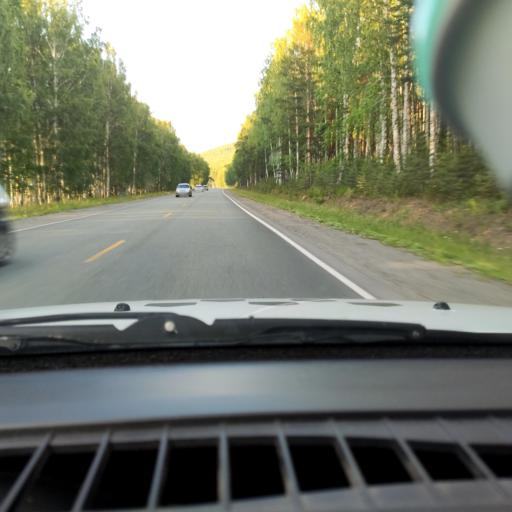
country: RU
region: Chelyabinsk
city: Karabash
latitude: 55.3209
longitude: 60.2206
